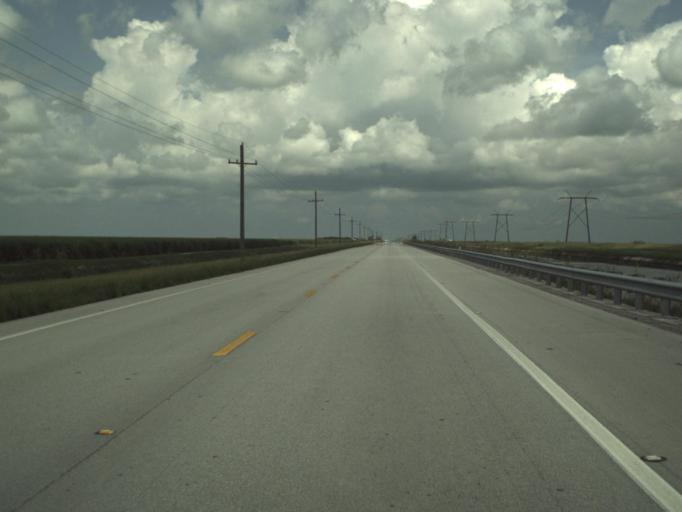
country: US
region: Florida
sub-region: Palm Beach County
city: Loxahatchee Groves
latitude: 26.7429
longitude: -80.4708
